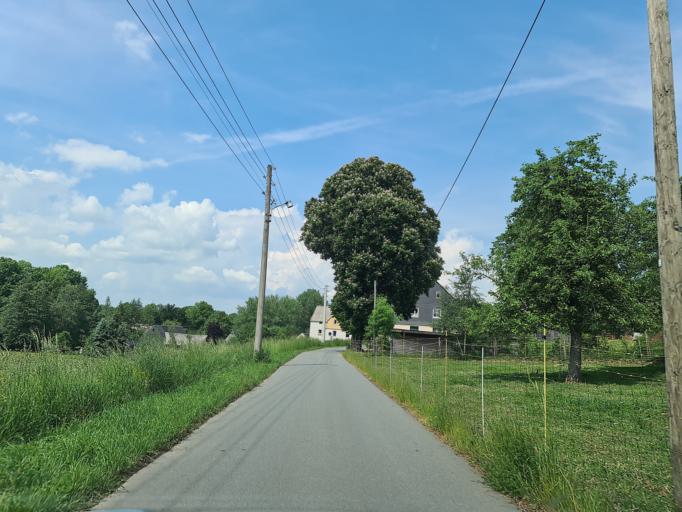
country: DE
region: Saxony
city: Stollberg
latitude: 50.6752
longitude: 12.7424
